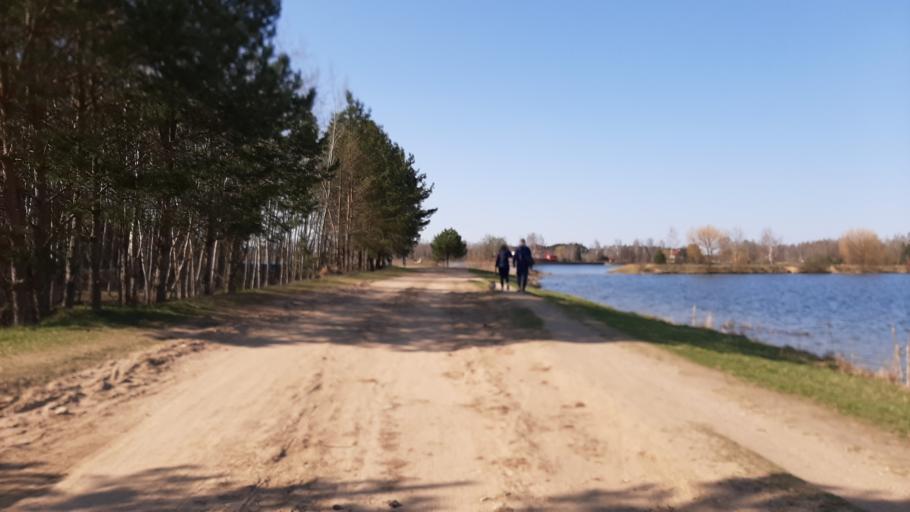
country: BY
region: Minsk
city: Bal'shavik
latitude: 53.9565
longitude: 27.5764
